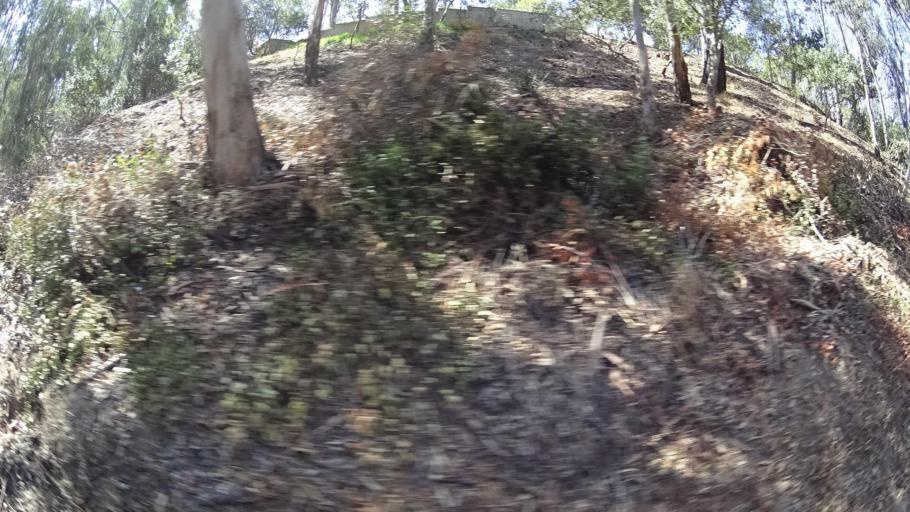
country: US
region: California
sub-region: San Diego County
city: Rancho Santa Fe
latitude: 33.0013
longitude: -117.2168
